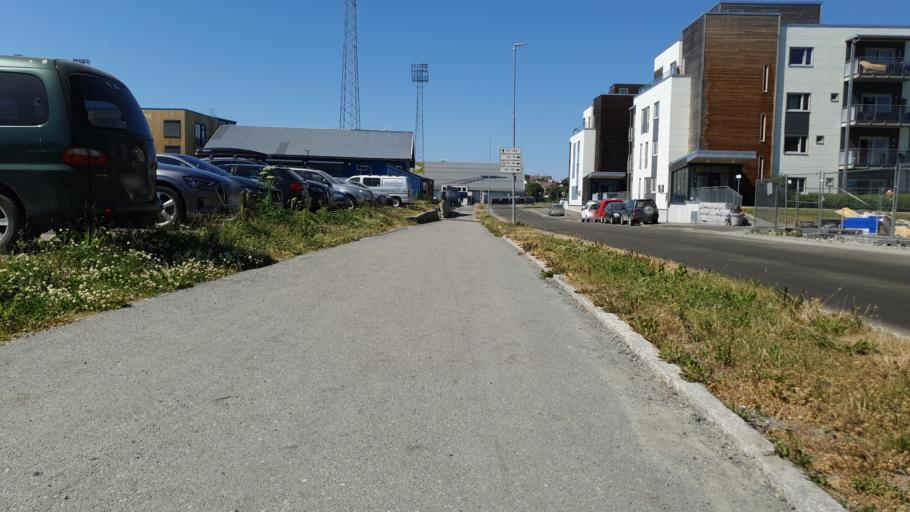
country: NO
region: Sor-Trondelag
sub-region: Trondheim
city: Trondheim
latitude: 63.4286
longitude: 10.5274
